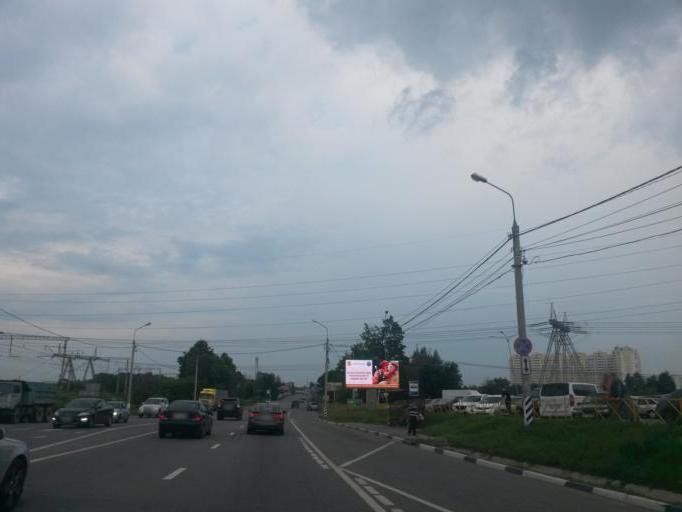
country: RU
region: Moskovskaya
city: Domodedovo
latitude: 55.4599
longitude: 37.7580
